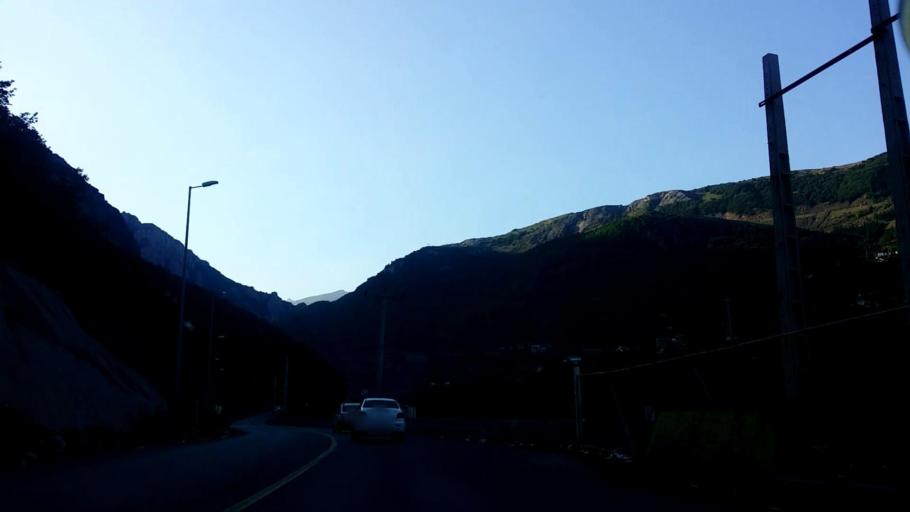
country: IR
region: Tehran
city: Tajrish
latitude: 36.2239
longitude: 51.3088
